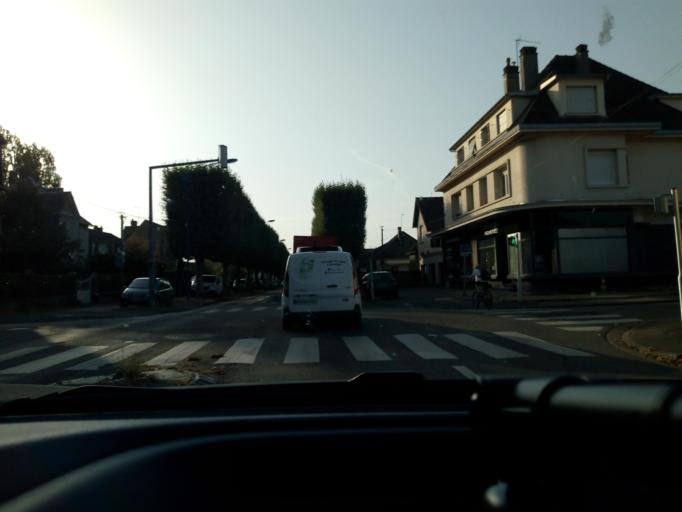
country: FR
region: Haute-Normandie
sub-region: Departement de la Seine-Maritime
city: Sotteville-les-Rouen
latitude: 49.4113
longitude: 1.0764
